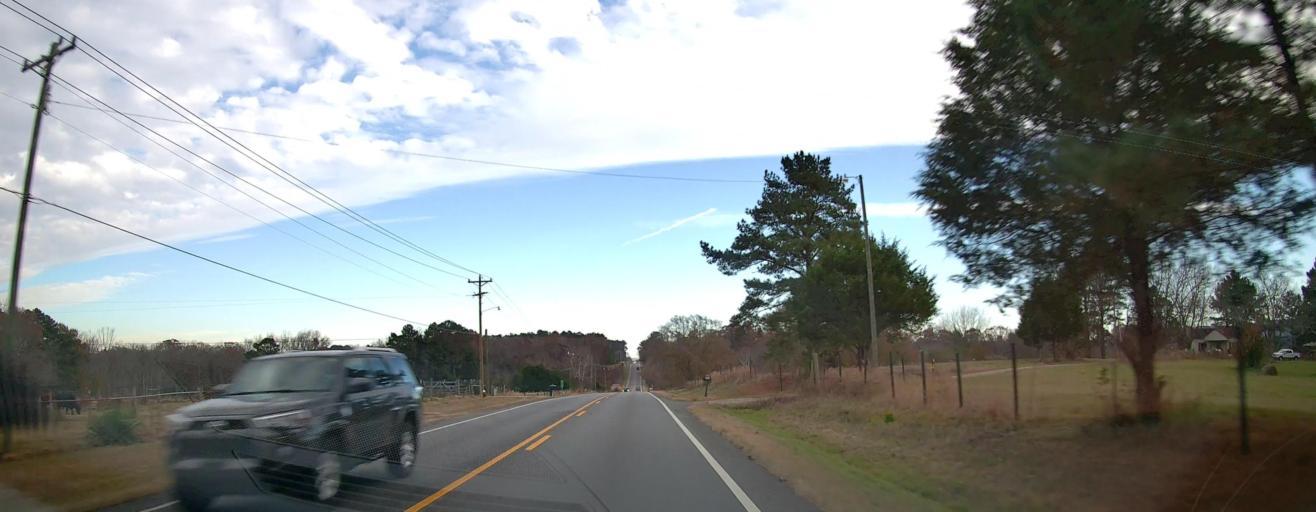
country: US
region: Alabama
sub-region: Morgan County
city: Priceville
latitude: 34.4551
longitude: -86.7705
